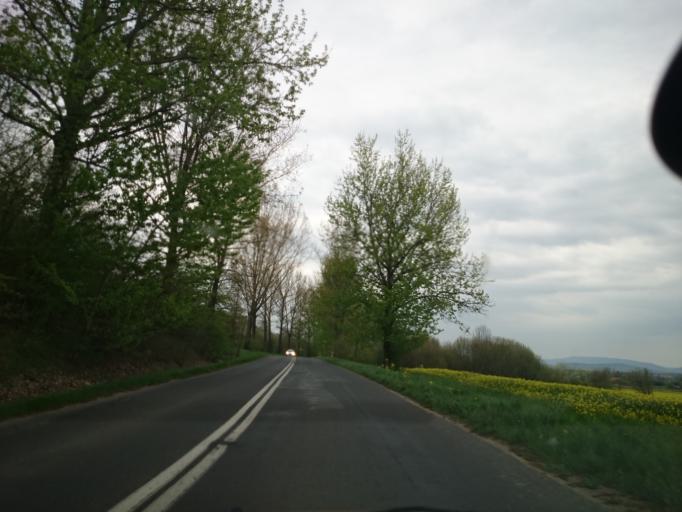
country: PL
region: Opole Voivodeship
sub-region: Powiat nyski
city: Nysa
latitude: 50.3953
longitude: 17.3449
